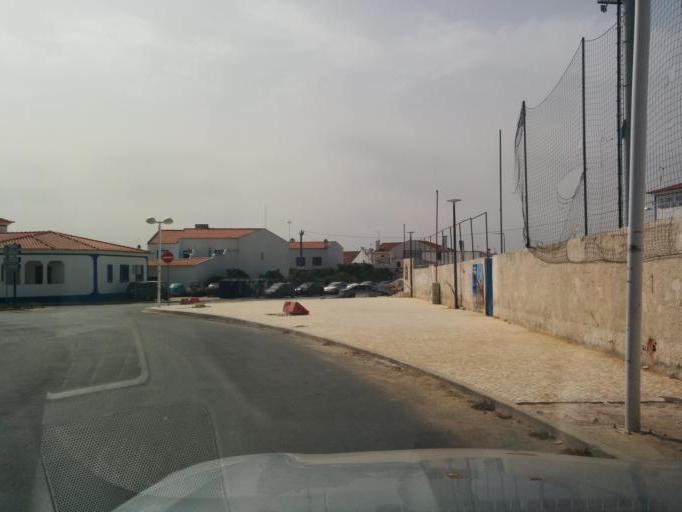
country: PT
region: Beja
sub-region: Odemira
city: Vila Nova de Milfontes
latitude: 37.7288
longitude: -8.7820
